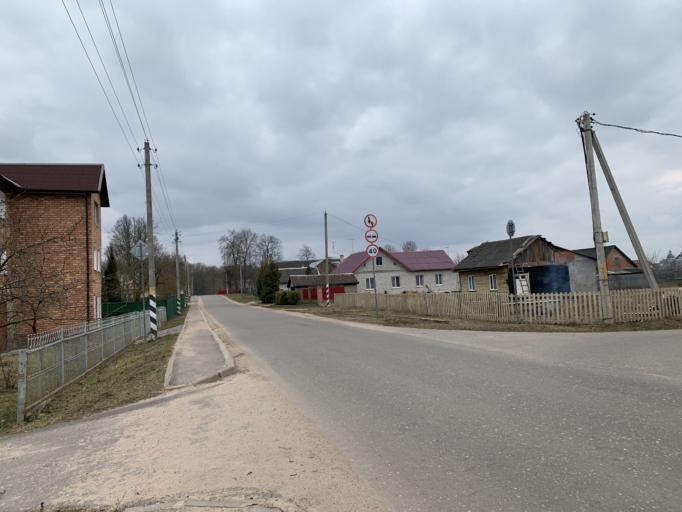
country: BY
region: Minsk
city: Nyasvizh
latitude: 53.2305
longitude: 26.6898
